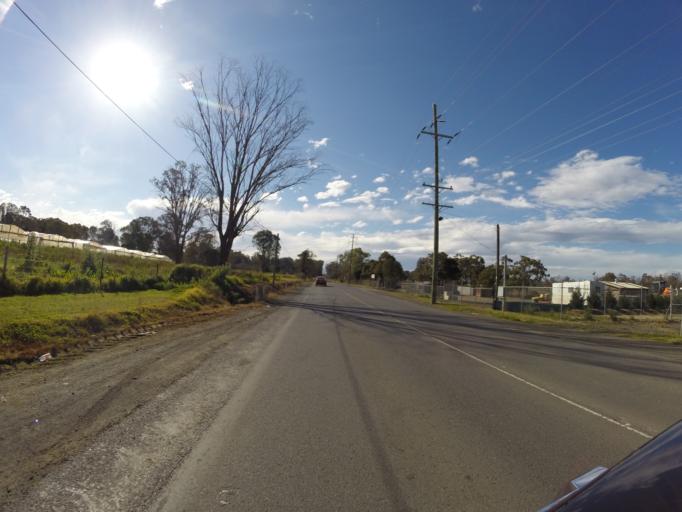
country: AU
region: New South Wales
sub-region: Liverpool
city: Bringelly
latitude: -33.9133
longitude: 150.7864
